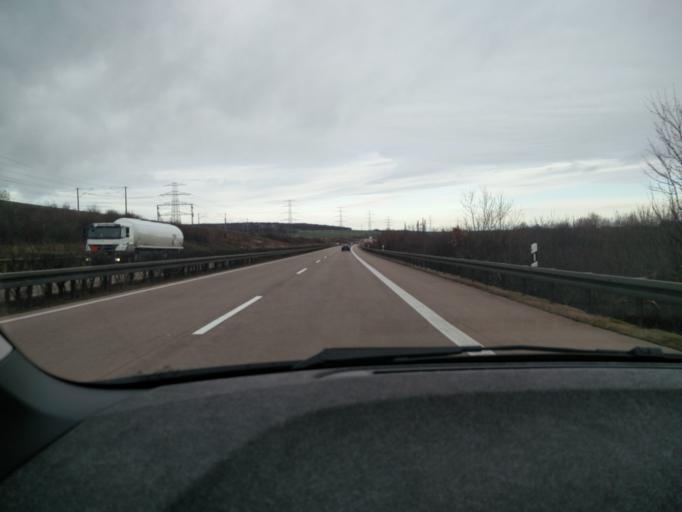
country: DE
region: Thuringia
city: Behringen
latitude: 50.7950
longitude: 11.0013
